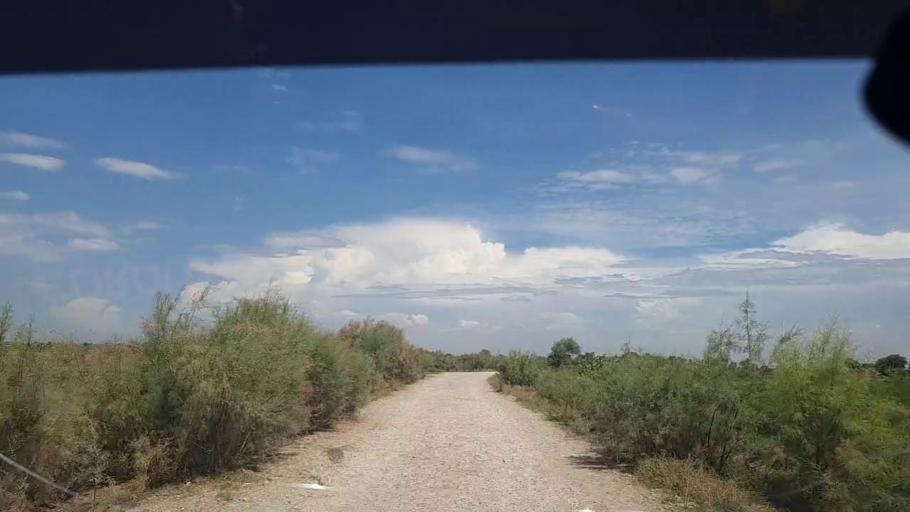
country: PK
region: Sindh
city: Ghauspur
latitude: 28.1476
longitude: 68.9751
